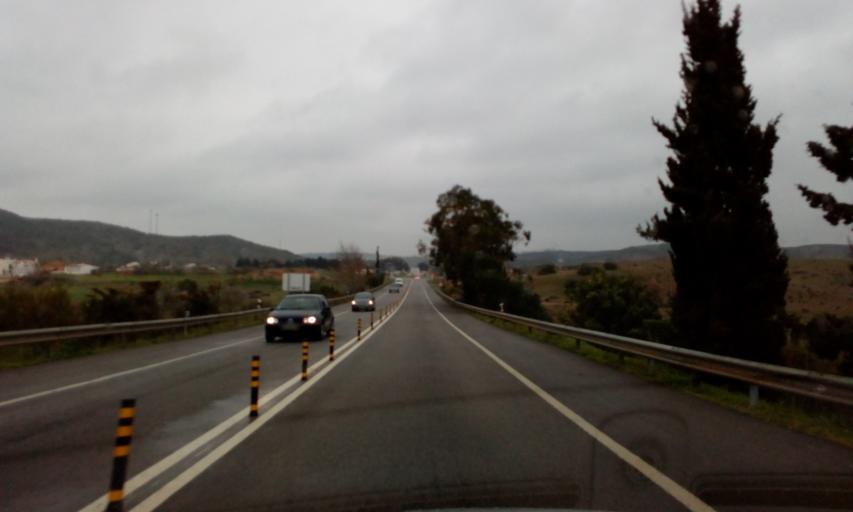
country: PT
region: Faro
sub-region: Vila do Bispo
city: Vila do Bispo
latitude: 37.0936
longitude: -8.8082
